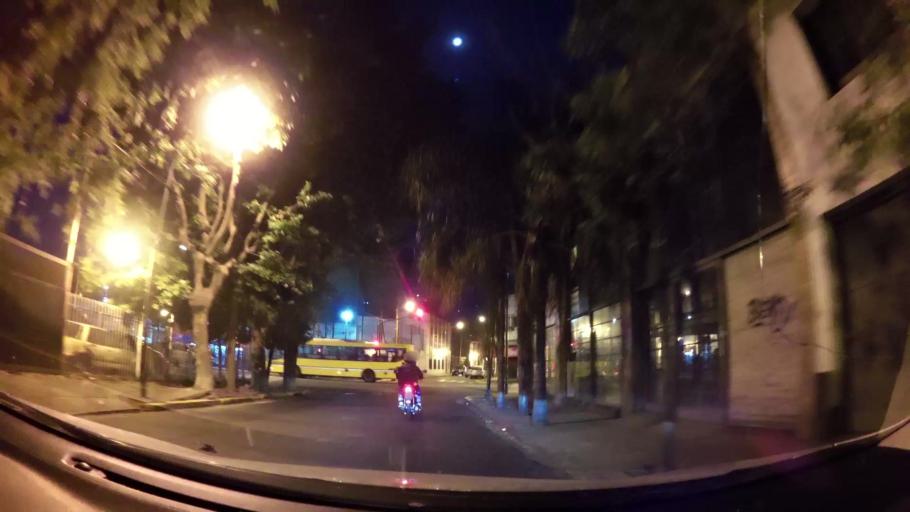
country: AR
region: Buenos Aires
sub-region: Partido de San Isidro
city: San Isidro
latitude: -34.4505
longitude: -58.5432
